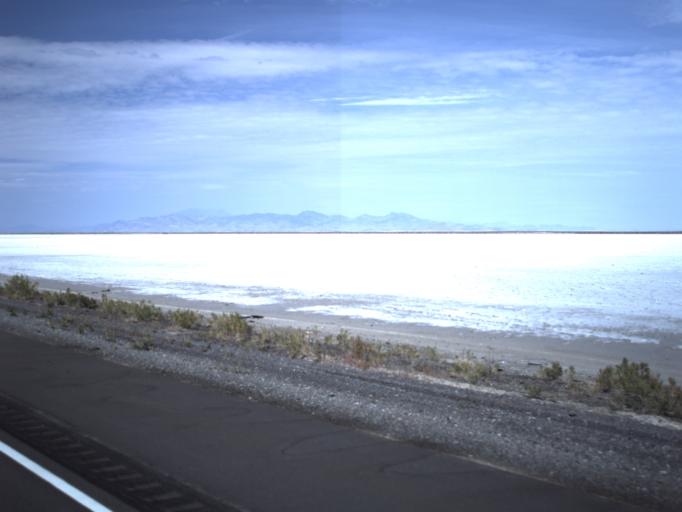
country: US
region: Utah
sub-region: Tooele County
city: Wendover
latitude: 40.7294
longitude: -113.3962
